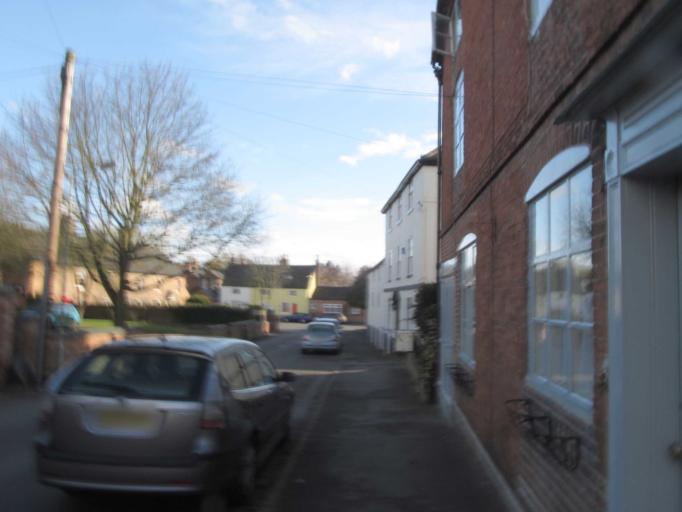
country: GB
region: England
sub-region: Leicestershire
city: Barrow upon Soar
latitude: 52.8050
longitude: -1.1060
